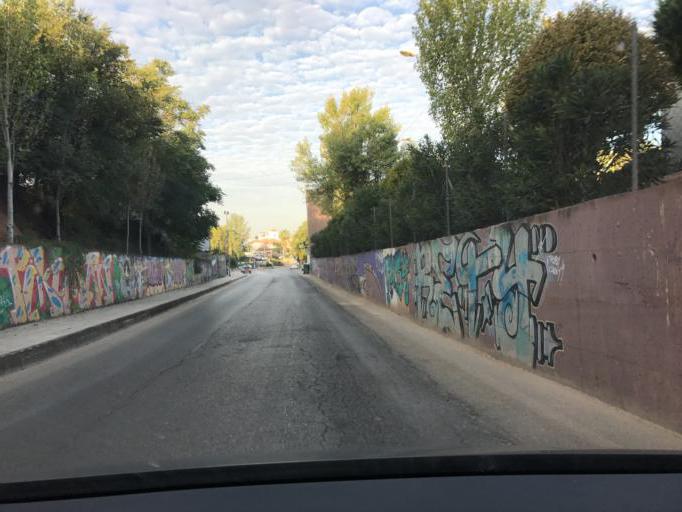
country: ES
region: Andalusia
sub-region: Provincia de Granada
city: Peligros
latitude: 37.2313
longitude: -3.6244
